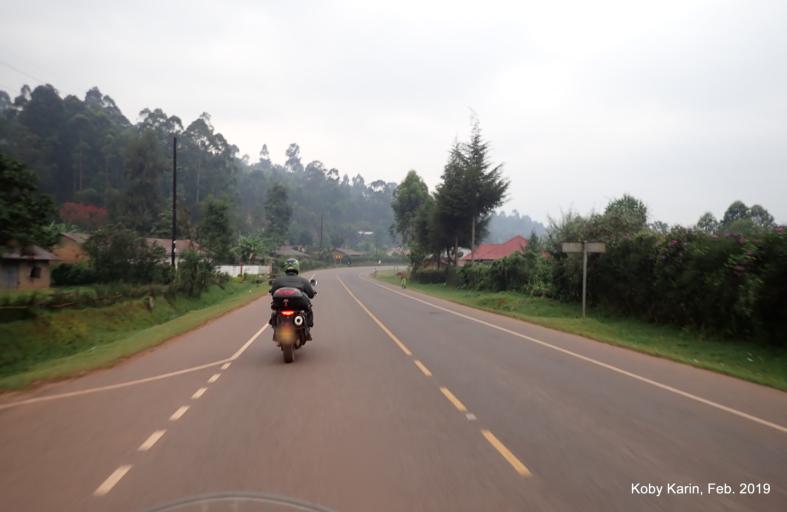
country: UG
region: Western Region
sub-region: Kabale District
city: Kabale
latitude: -1.2443
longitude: 29.9728
